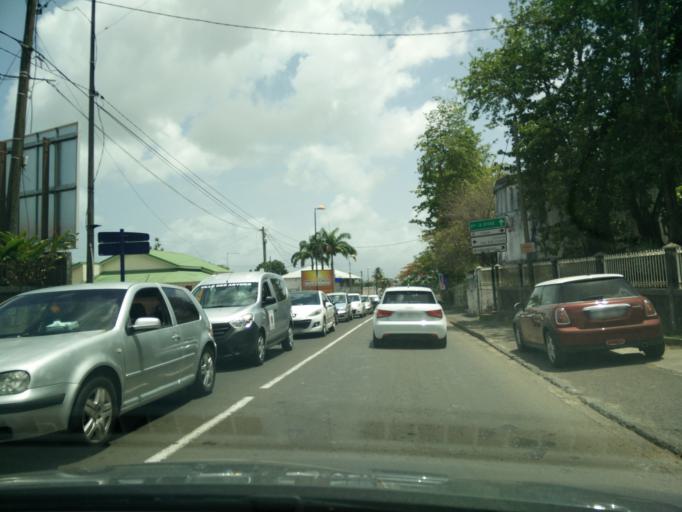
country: GP
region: Guadeloupe
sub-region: Guadeloupe
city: Les Abymes
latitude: 16.2670
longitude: -61.5087
